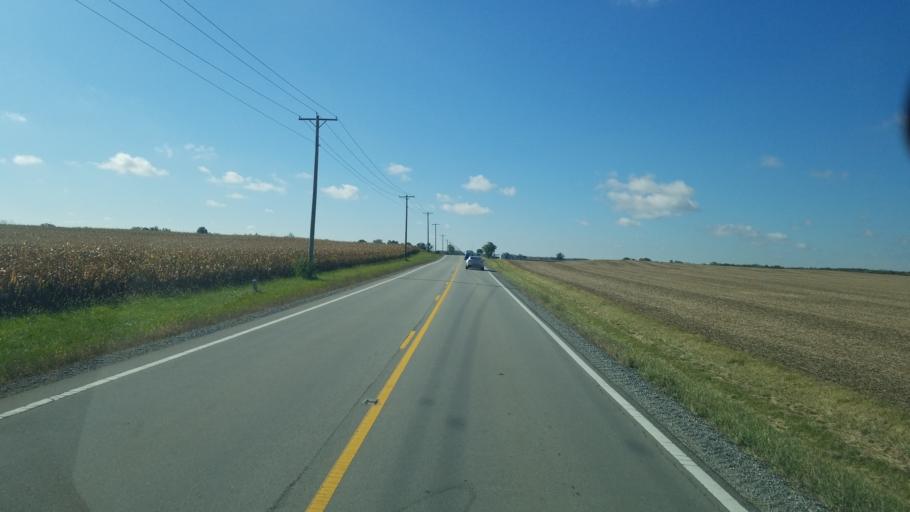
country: US
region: Ohio
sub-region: Highland County
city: Leesburg
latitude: 39.4137
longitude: -83.5240
